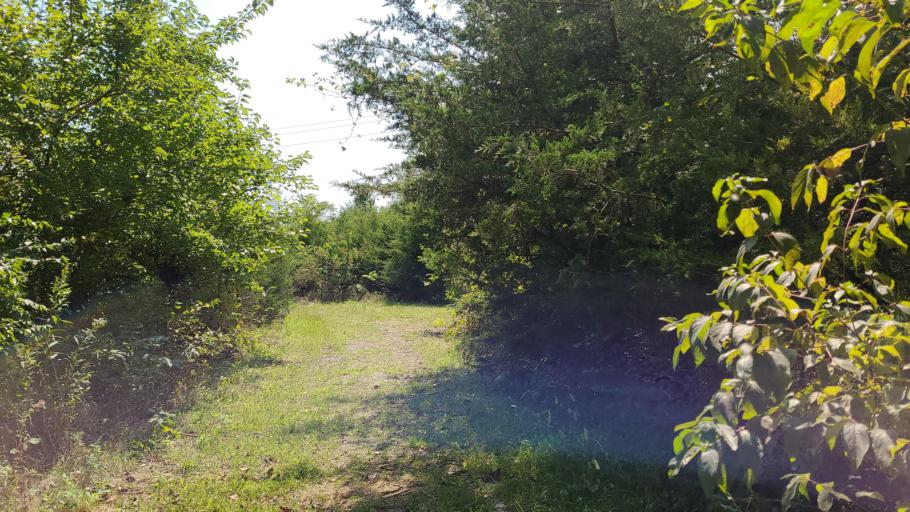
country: US
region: Kansas
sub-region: Douglas County
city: Lawrence
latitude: 38.9577
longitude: -95.3179
